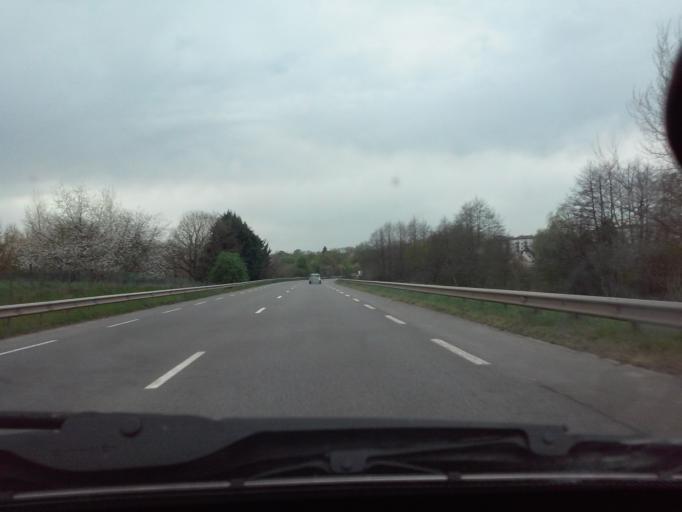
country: FR
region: Brittany
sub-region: Departement d'Ille-et-Vilaine
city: Fougeres
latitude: 48.3372
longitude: -1.2037
